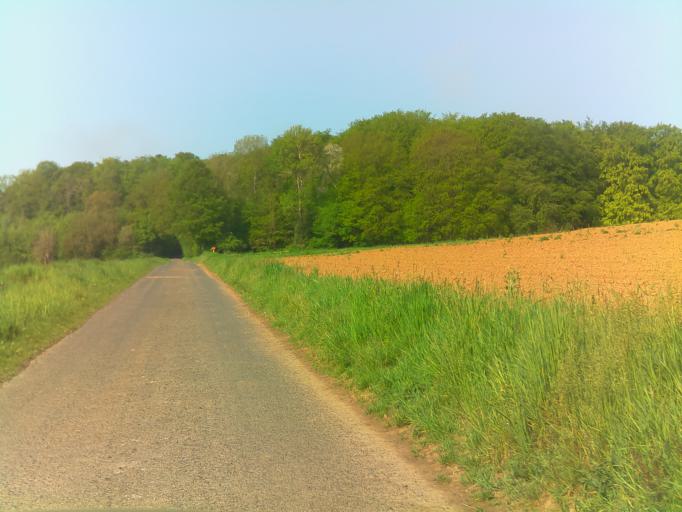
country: DE
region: Hesse
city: Hain-Grundau
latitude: 50.2292
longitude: 9.0868
